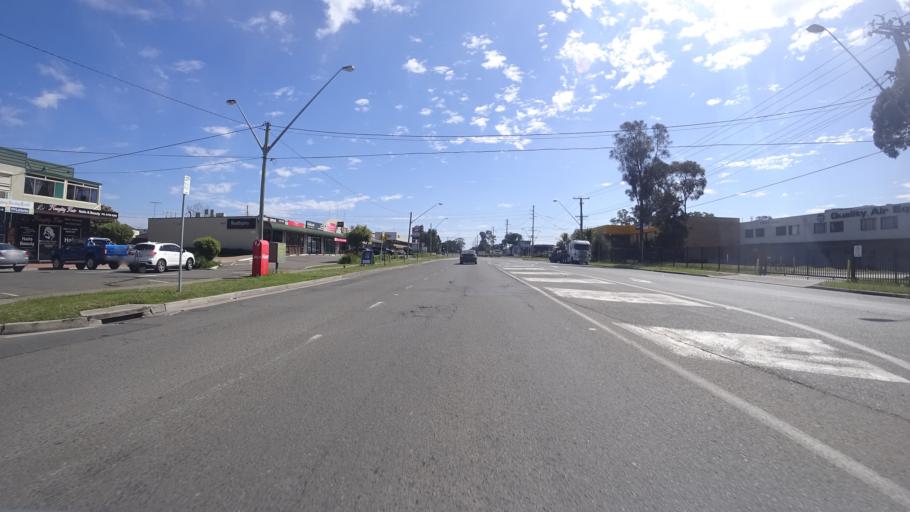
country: AU
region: New South Wales
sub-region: Bankstown
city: Milperra
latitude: -33.9242
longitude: 150.9621
